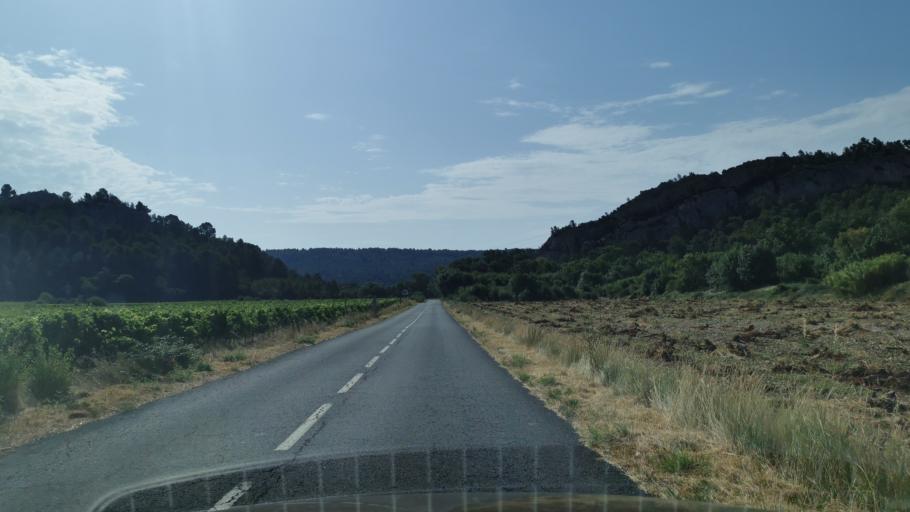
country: FR
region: Languedoc-Roussillon
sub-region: Departement de l'Aude
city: Bize-Minervois
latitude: 43.3453
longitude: 2.8619
